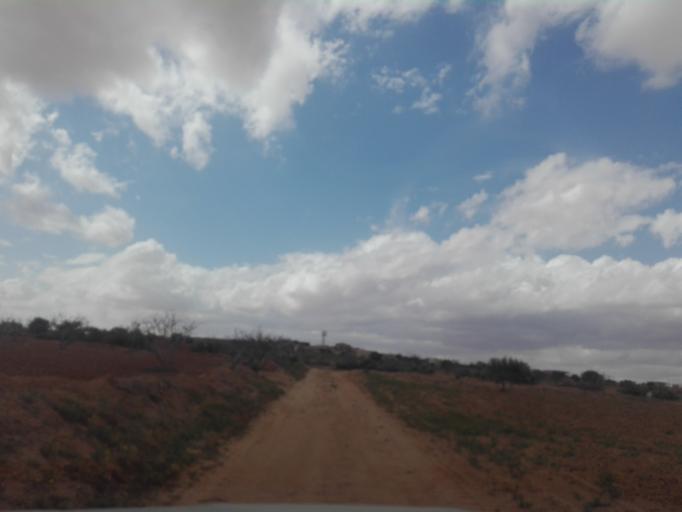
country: TN
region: Safaqis
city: Sfax
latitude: 34.7010
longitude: 10.4409
